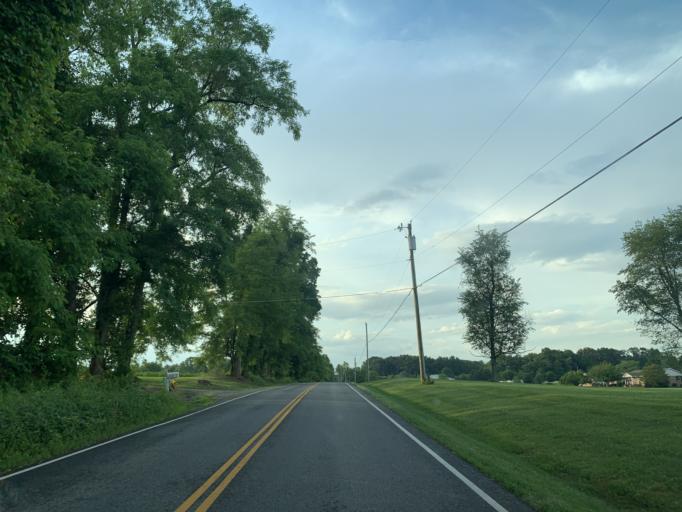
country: US
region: Maryland
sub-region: Cecil County
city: Rising Sun
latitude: 39.7090
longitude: -76.0470
